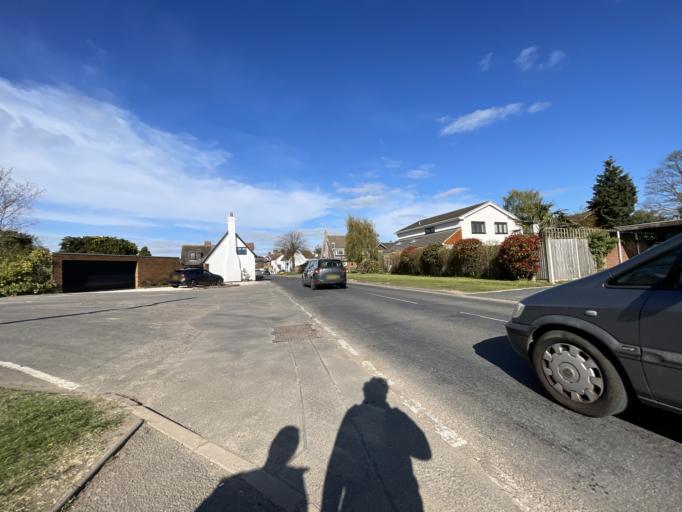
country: GB
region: England
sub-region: Warwickshire
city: Dunchurch
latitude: 52.3351
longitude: -1.2928
